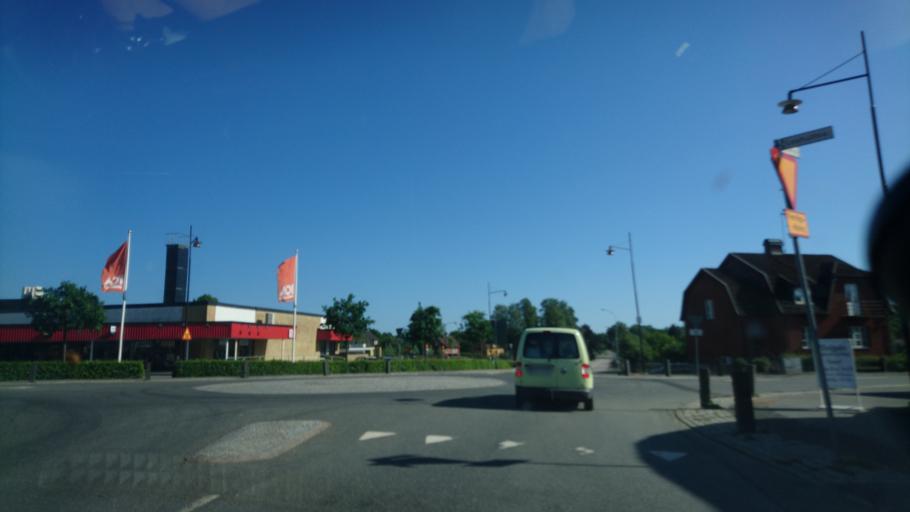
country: SE
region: Skane
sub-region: Osby Kommun
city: Lonsboda
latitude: 56.3977
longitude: 14.3201
